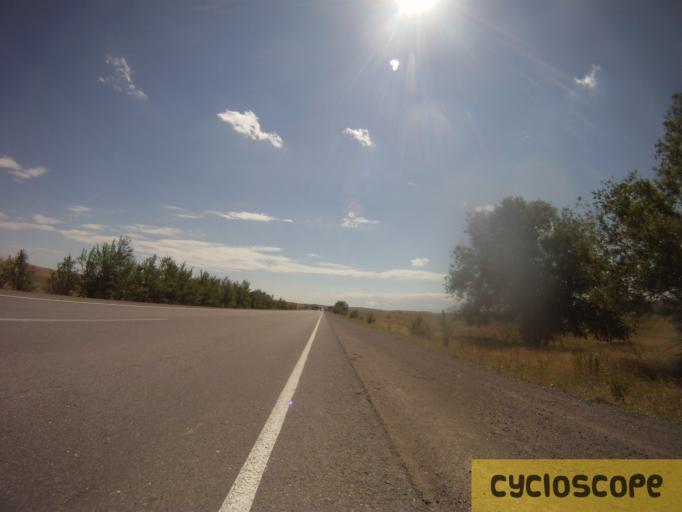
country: KG
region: Chuy
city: Bystrovka
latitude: 43.3263
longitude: 75.9077
